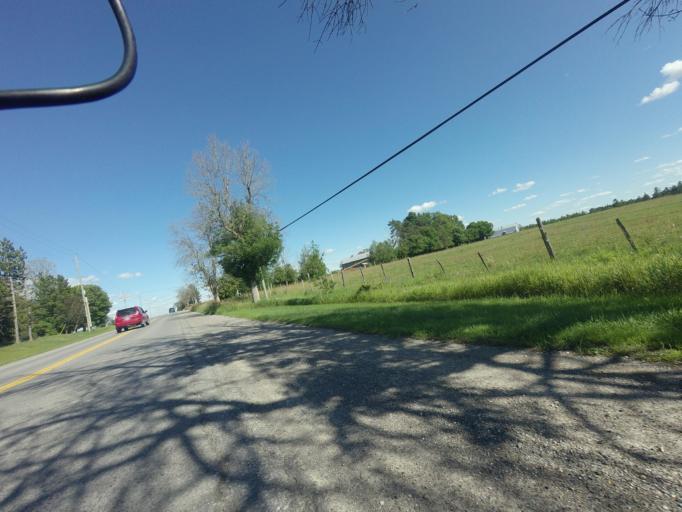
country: CA
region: Ontario
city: Arnprior
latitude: 45.4170
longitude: -76.4227
